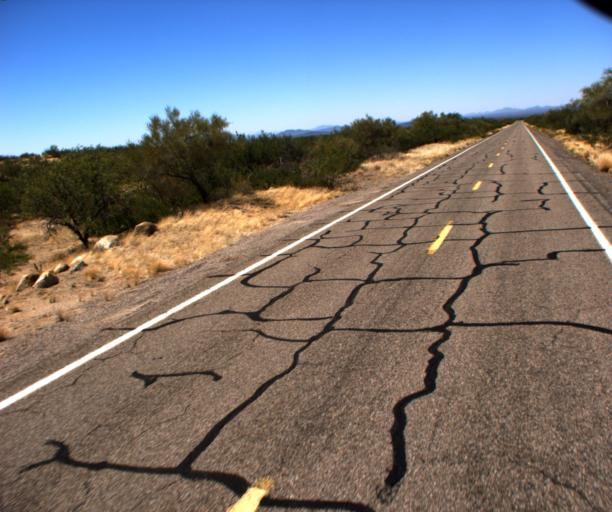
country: US
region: Arizona
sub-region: Pima County
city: Three Points
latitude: 32.0155
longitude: -111.5754
